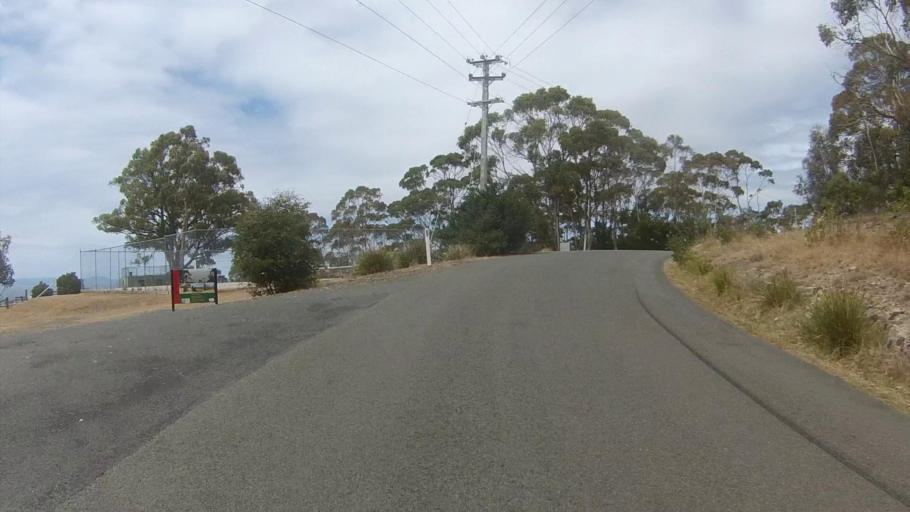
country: AU
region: Tasmania
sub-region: Kingborough
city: Blackmans Bay
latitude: -43.0504
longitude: 147.3404
